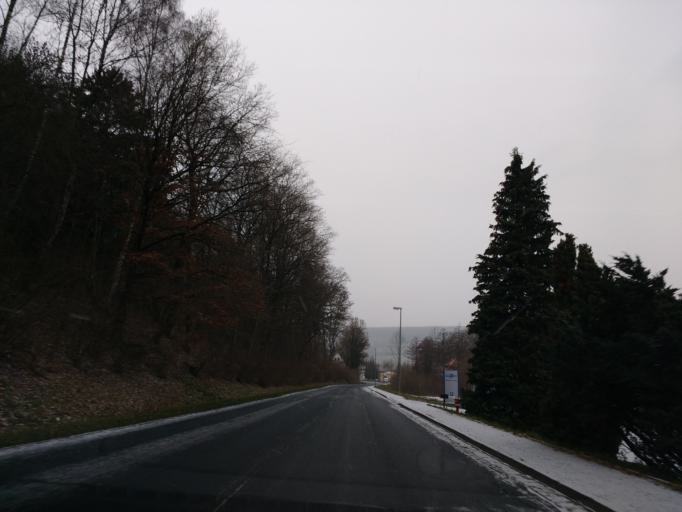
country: DE
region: Hesse
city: Spangenberg
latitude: 51.1134
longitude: 9.6707
